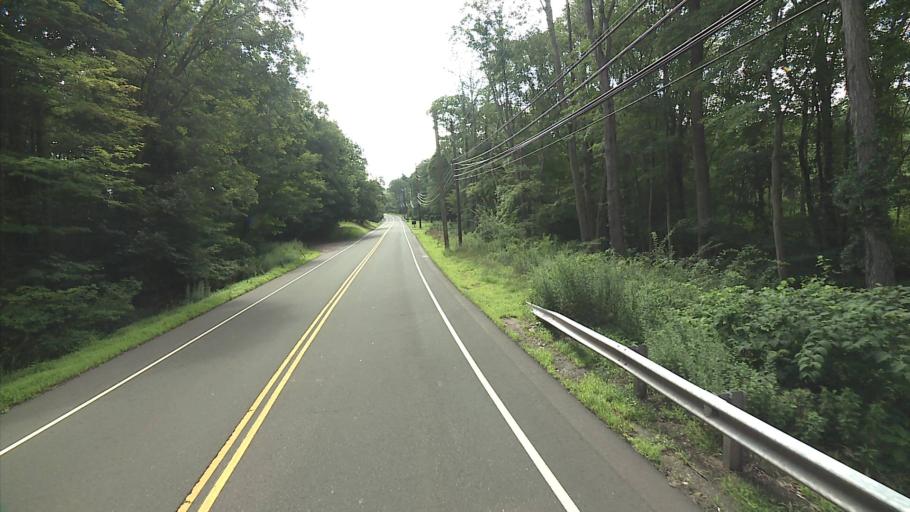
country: US
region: Connecticut
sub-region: New Haven County
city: Woodbridge
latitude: 41.3304
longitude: -73.0321
